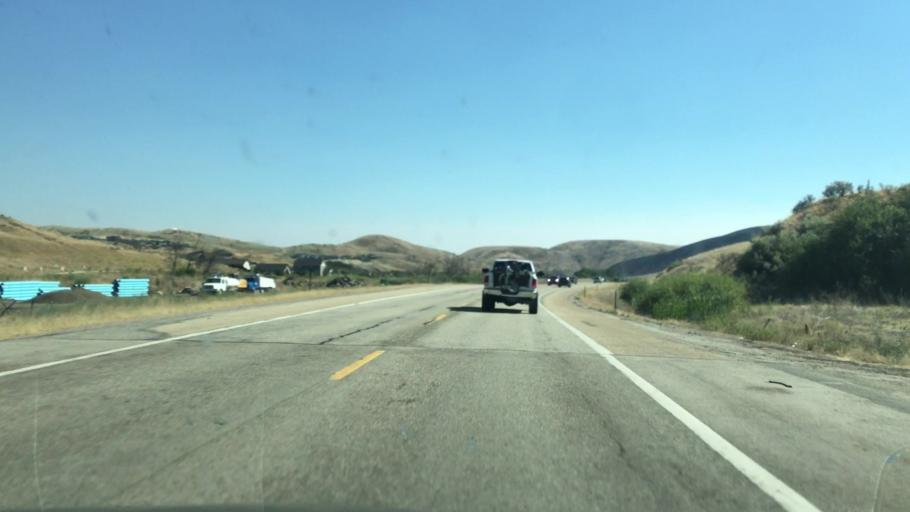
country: US
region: Idaho
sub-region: Ada County
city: Eagle
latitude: 43.7845
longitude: -116.2632
